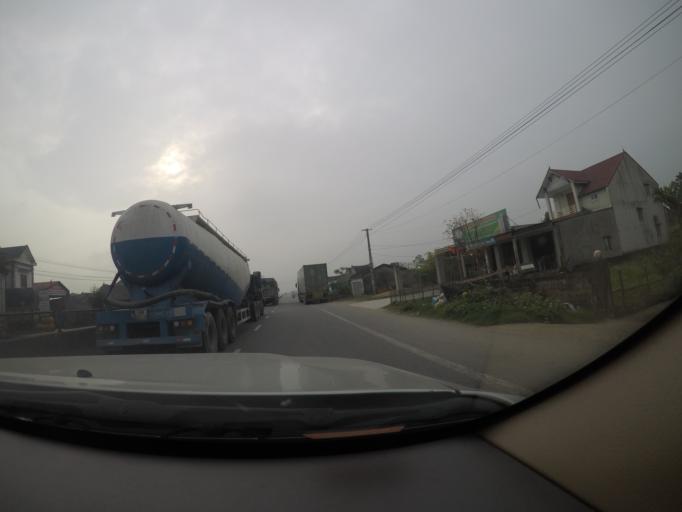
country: VN
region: Ha Tinh
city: Ky Anh
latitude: 18.1922
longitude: 106.1804
